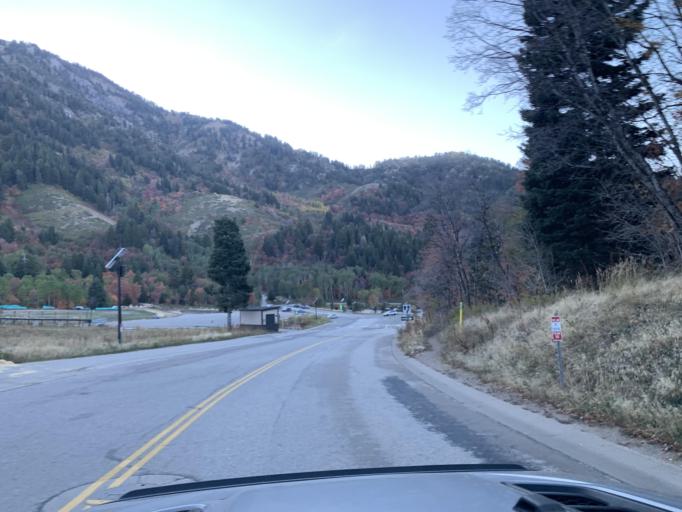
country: US
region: Utah
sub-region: Weber County
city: Uintah
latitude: 41.2169
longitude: -111.8591
